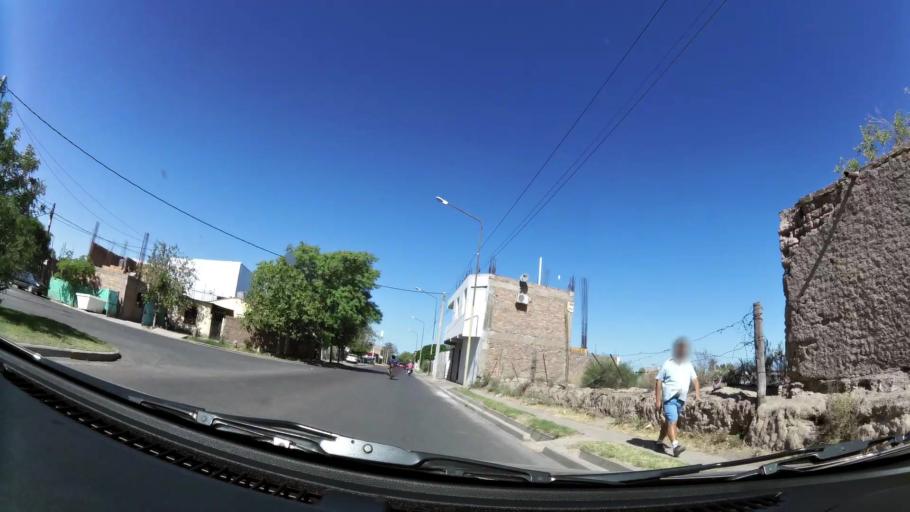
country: AR
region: San Juan
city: San Juan
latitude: -31.5440
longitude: -68.5450
